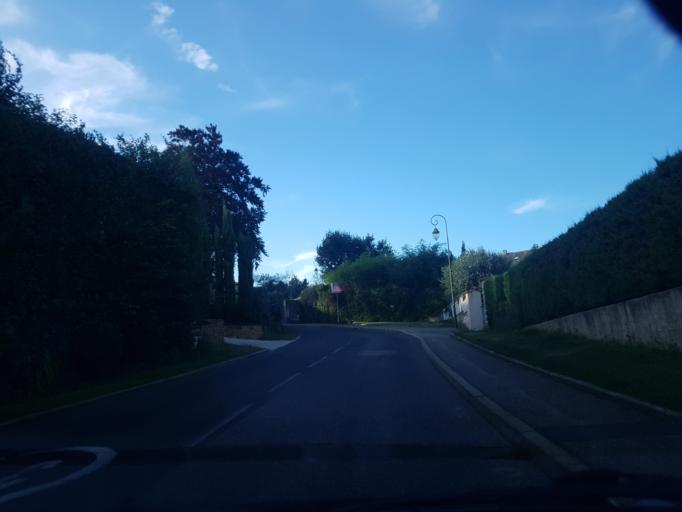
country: FR
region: Rhone-Alpes
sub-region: Departement du Rhone
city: Villefranche-sur-Saone
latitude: 45.9729
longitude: 4.7139
